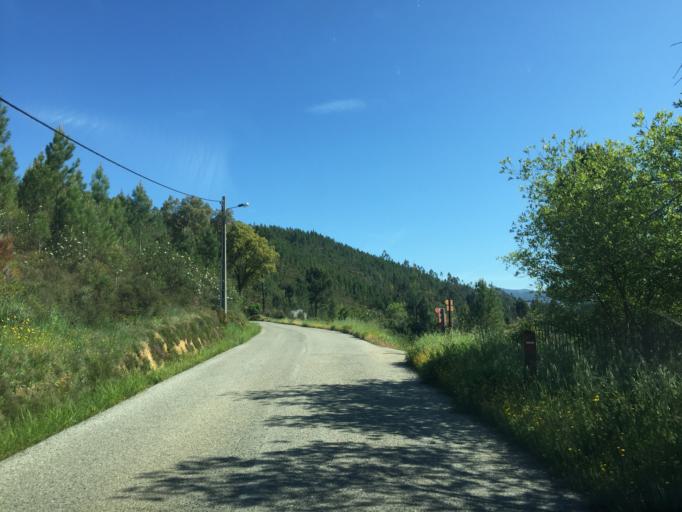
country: PT
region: Coimbra
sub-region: Pampilhosa da Serra
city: Pampilhosa da Serra
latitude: 40.0503
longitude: -7.8116
